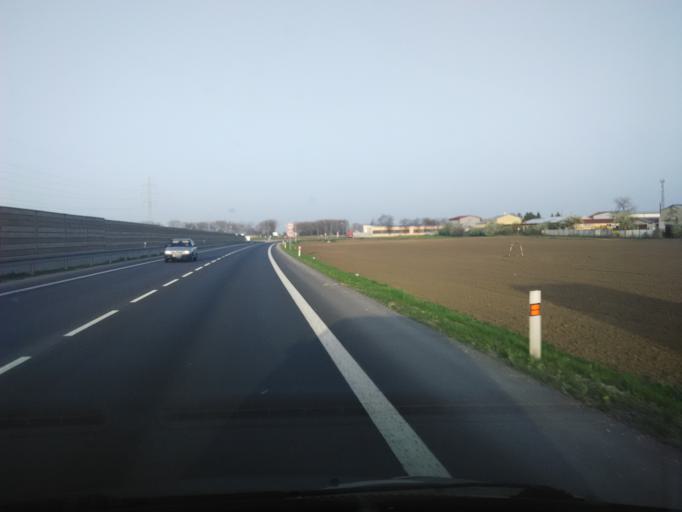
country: SK
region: Trnavsky
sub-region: Okres Galanta
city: Galanta
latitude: 48.1786
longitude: 17.7336
